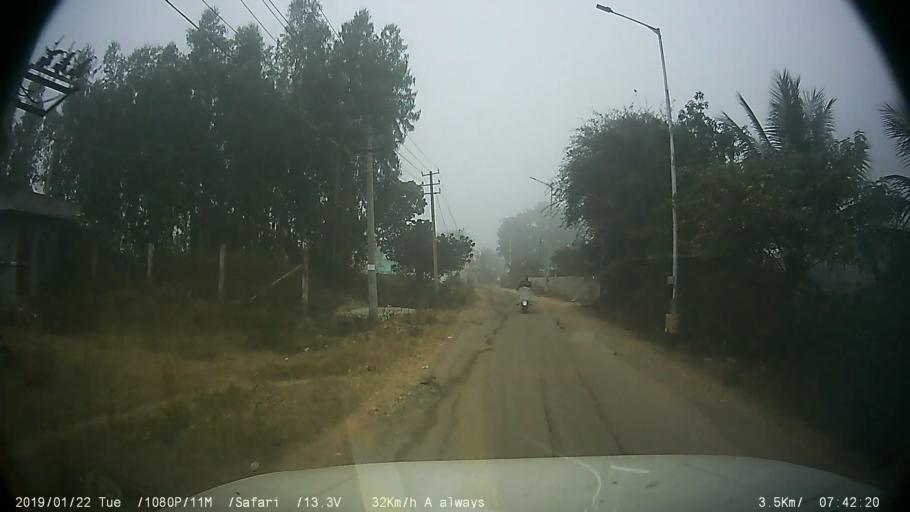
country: IN
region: Karnataka
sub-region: Bangalore Urban
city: Anekal
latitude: 12.8260
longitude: 77.6338
